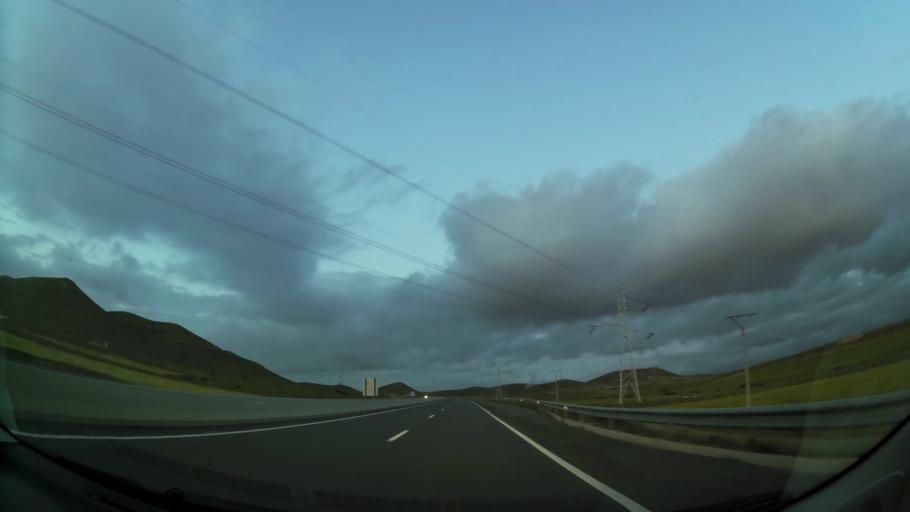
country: MA
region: Oriental
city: El Aioun
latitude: 34.6146
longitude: -2.4295
